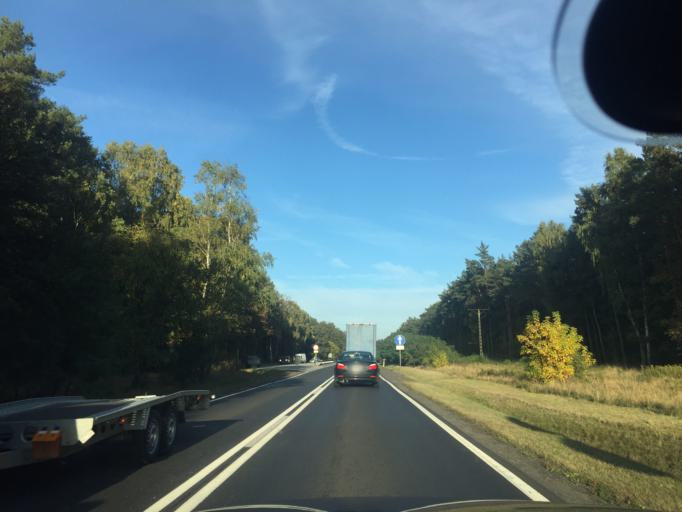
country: PL
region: Kujawsko-Pomorskie
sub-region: Powiat inowroclawski
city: Gniewkowo
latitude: 52.9147
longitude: 18.4878
